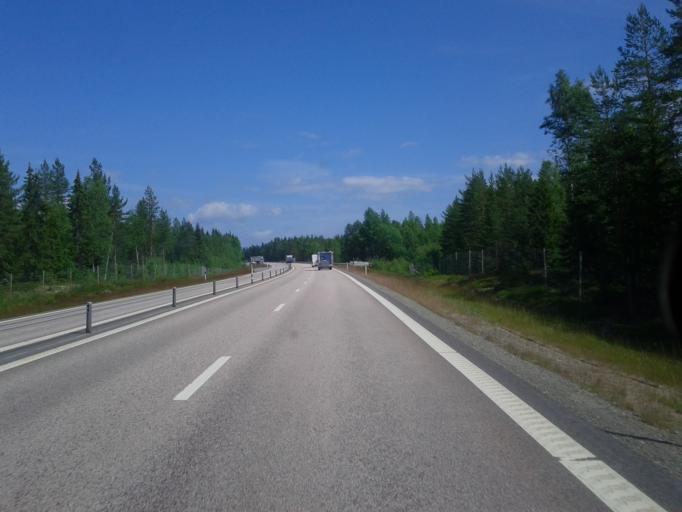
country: SE
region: Vaesternorrland
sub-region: OErnskoeldsviks Kommun
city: Husum
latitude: 63.4709
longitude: 19.2806
